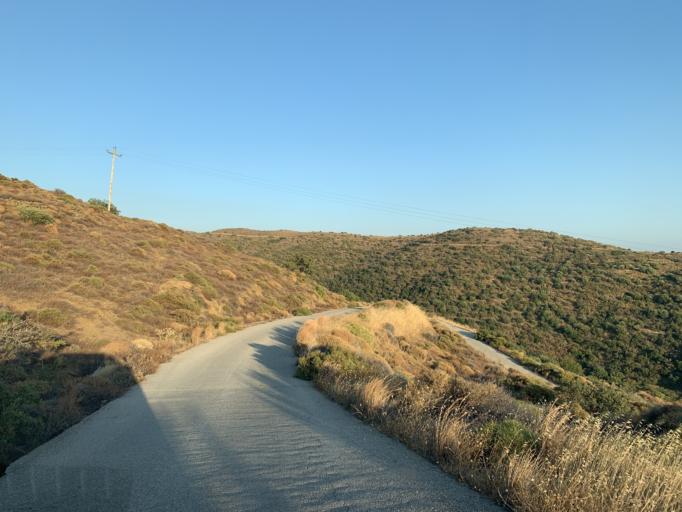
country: GR
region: North Aegean
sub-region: Chios
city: Psara
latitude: 38.5243
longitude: 25.8517
